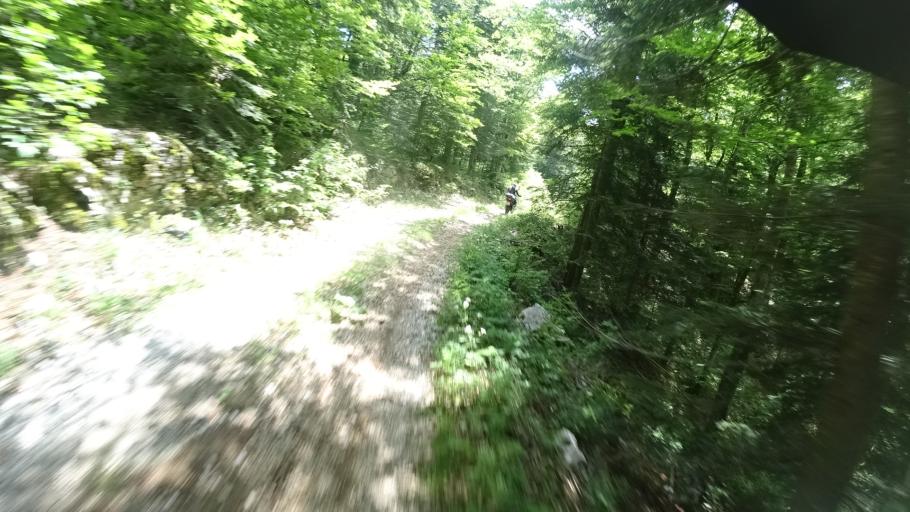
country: HR
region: Zadarska
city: Gracac
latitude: 44.4762
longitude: 15.8940
